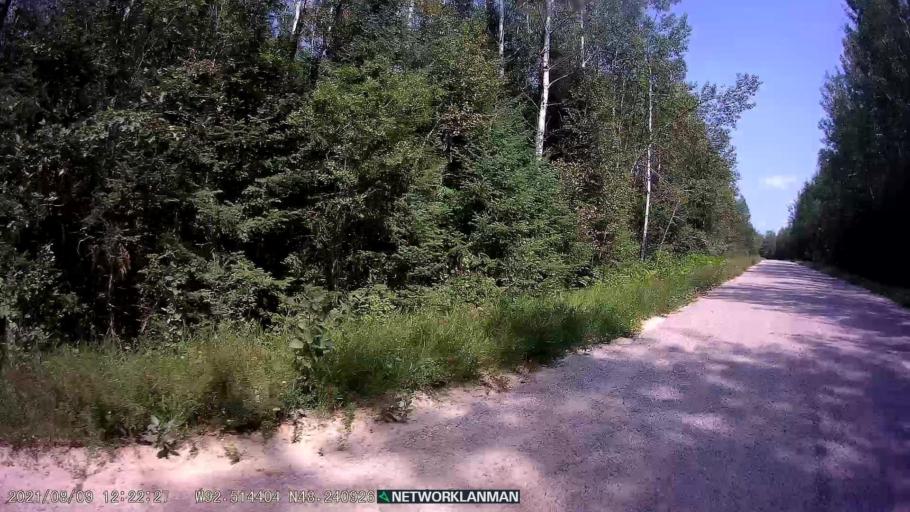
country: US
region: Minnesota
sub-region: Saint Louis County
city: Parkville
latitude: 48.2409
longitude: -92.5140
